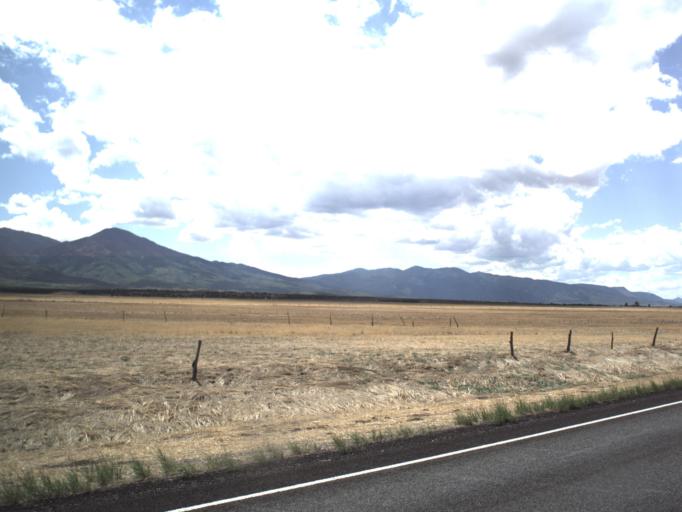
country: US
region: Utah
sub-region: Millard County
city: Fillmore
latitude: 39.1276
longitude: -112.2528
